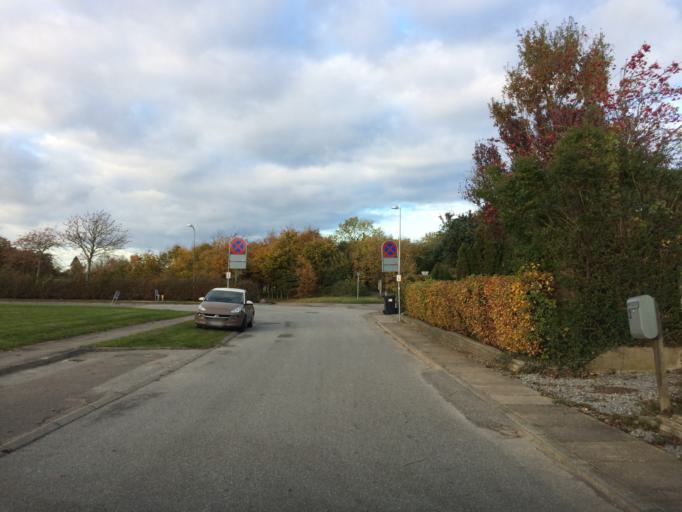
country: DK
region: South Denmark
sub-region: Sonderborg Kommune
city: Nordborg
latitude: 55.0398
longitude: 9.7949
